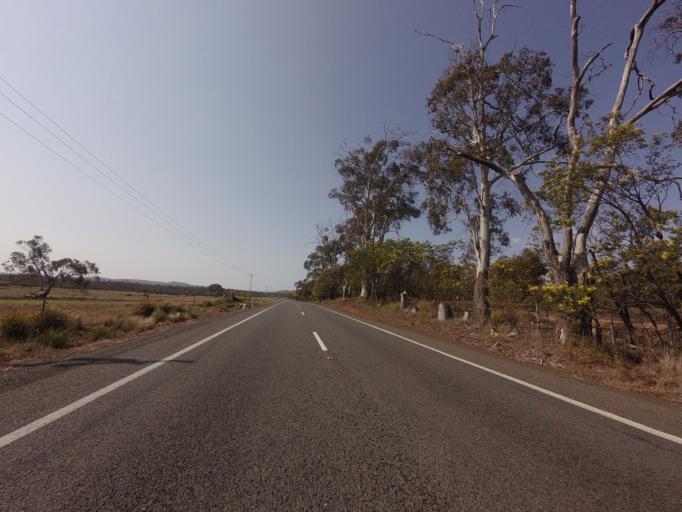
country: AU
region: Tasmania
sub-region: Northern Midlands
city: Evandale
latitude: -41.8318
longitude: 147.4790
